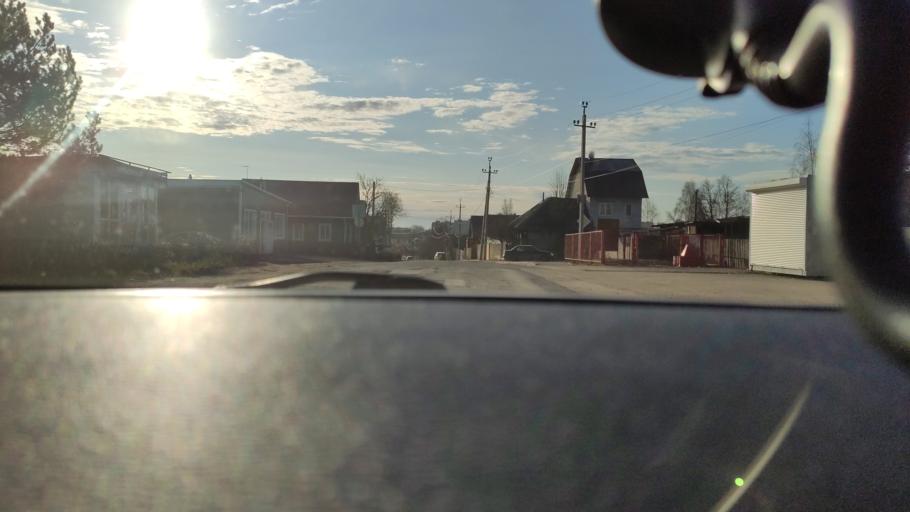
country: RU
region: Perm
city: Kondratovo
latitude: 58.0534
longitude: 56.0284
